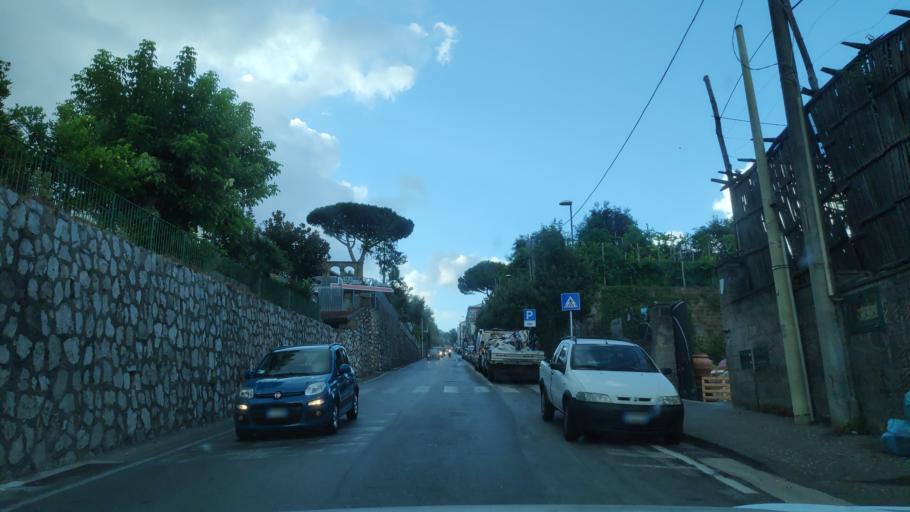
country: IT
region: Campania
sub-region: Provincia di Napoli
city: Piano di Sorrento
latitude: 40.6345
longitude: 14.4171
